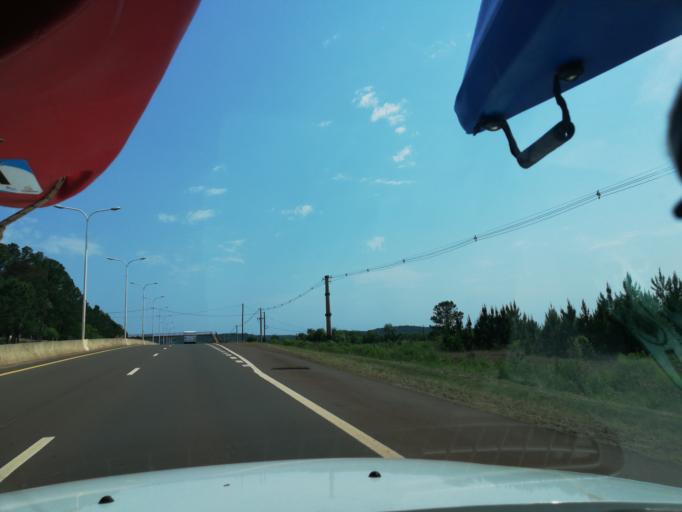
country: AR
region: Misiones
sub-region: Departamento de Candelaria
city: Loreto
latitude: -27.2987
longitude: -55.5364
